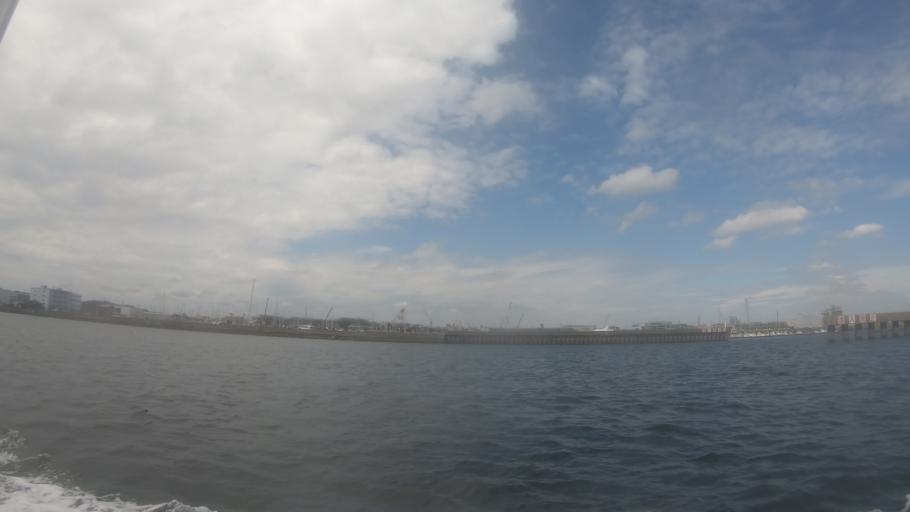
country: JP
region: Kanagawa
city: Yokohama
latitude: 35.3780
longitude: 139.6536
